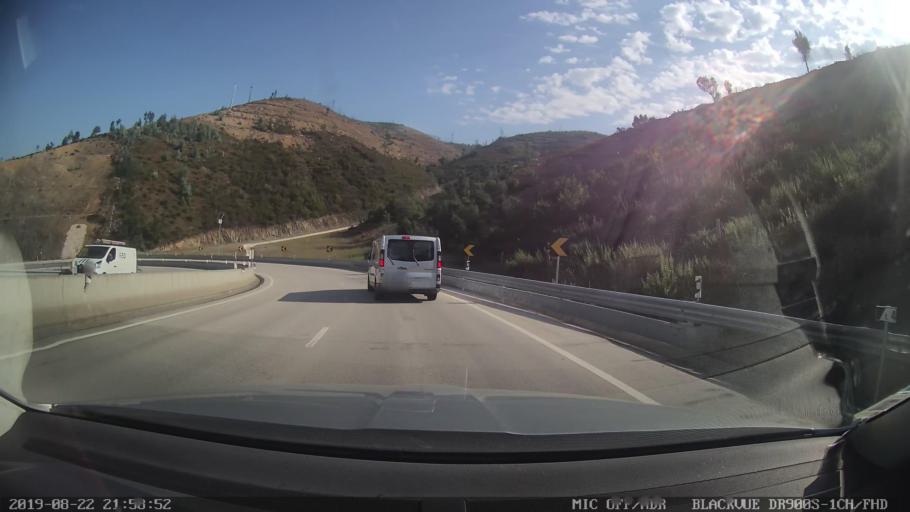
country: PT
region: Coimbra
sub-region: Coimbra
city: Coimbra
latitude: 40.1803
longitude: -8.3892
